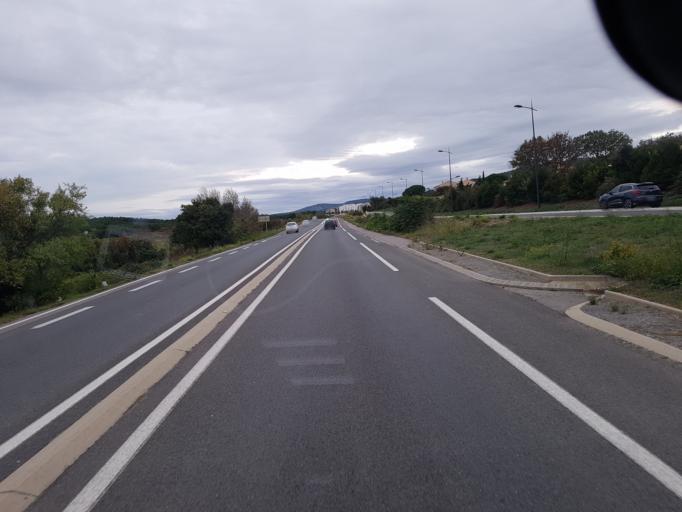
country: FR
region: Languedoc-Roussillon
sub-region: Departement de l'Aude
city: Peyriac-de-Mer
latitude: 43.1384
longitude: 2.9710
